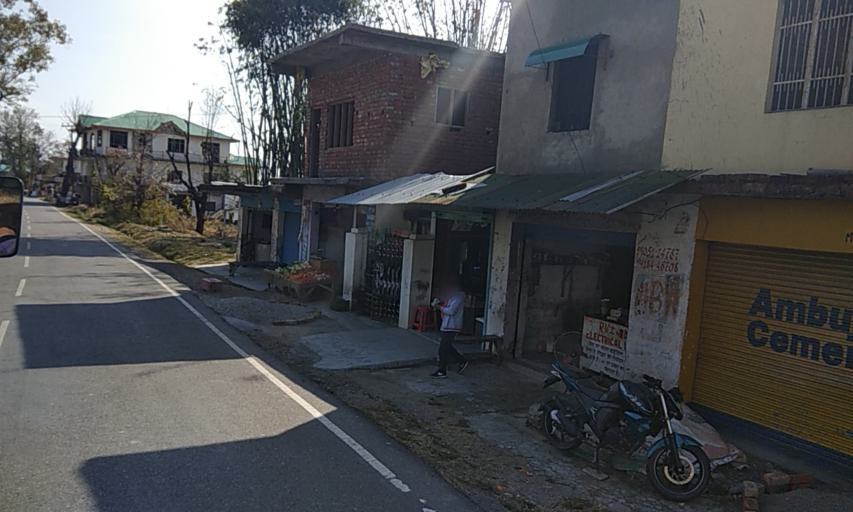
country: IN
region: Himachal Pradesh
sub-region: Kangra
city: Dharmsala
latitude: 32.1697
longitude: 76.3906
